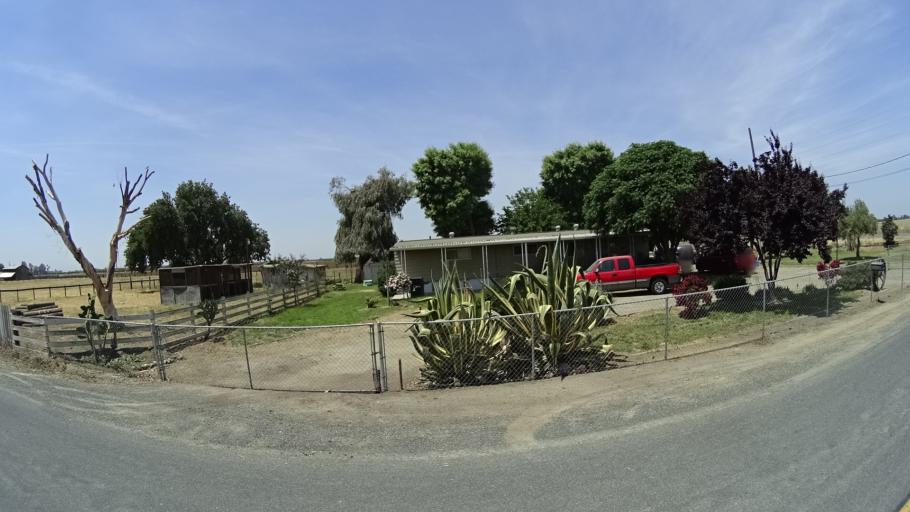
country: US
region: California
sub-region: Fresno County
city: Riverdale
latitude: 36.4016
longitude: -119.8341
